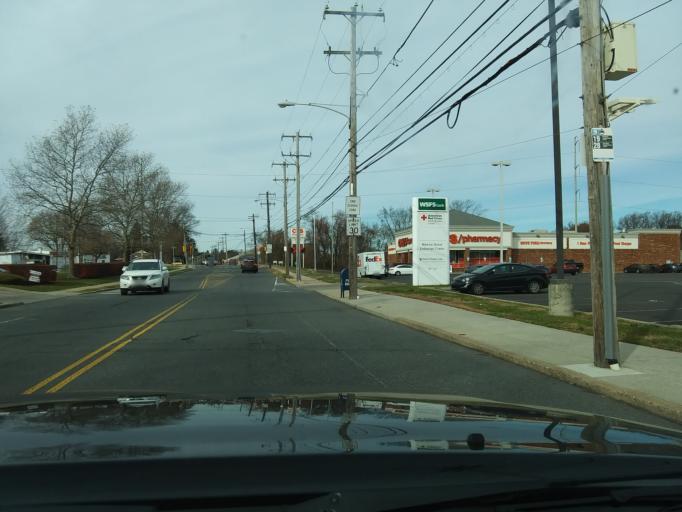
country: US
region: Pennsylvania
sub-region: Montgomery County
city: Rockledge
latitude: 40.0681
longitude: -75.0661
